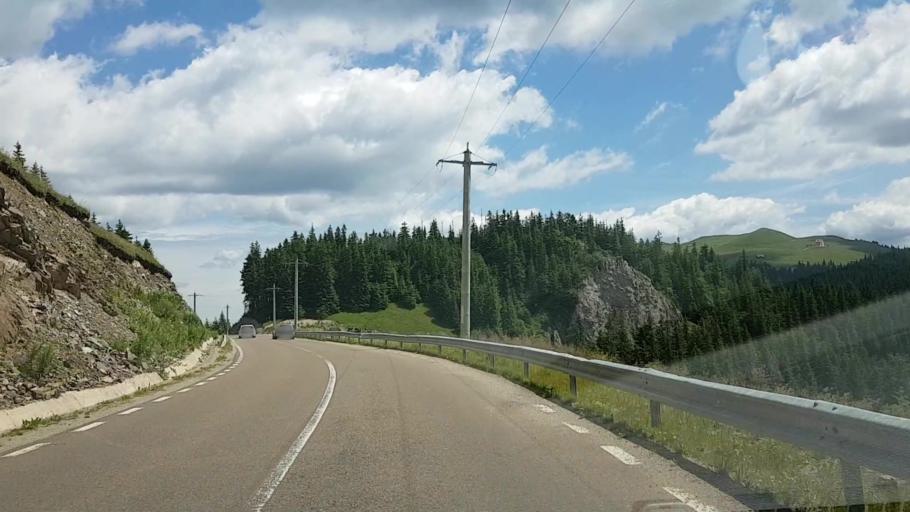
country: RO
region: Suceava
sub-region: Municipiul Campulung Moldovenesc
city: Campulung Moldovenesc
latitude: 47.4536
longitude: 25.5452
